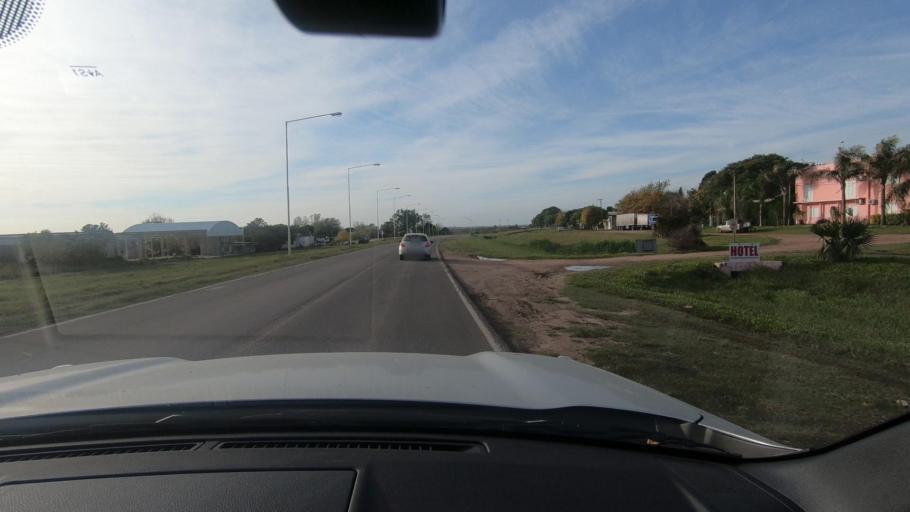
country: AR
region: Entre Rios
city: Colon
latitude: -32.2585
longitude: -58.2321
